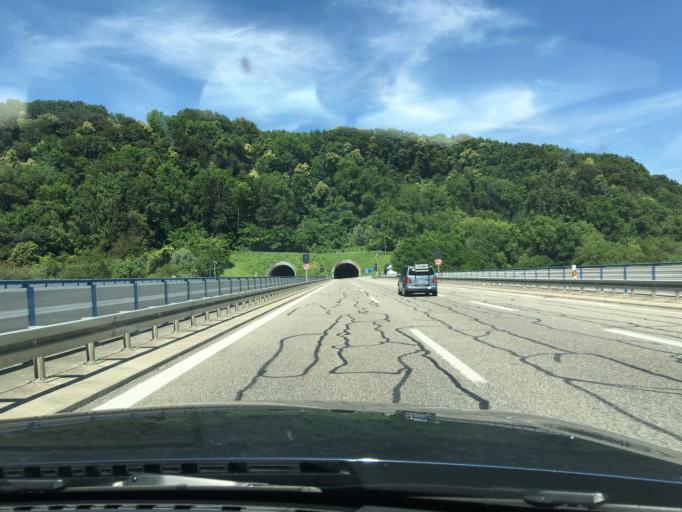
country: DE
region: Baden-Wuerttemberg
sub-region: Freiburg Region
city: Rheinfelden (Baden)
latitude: 47.5693
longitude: 7.7607
